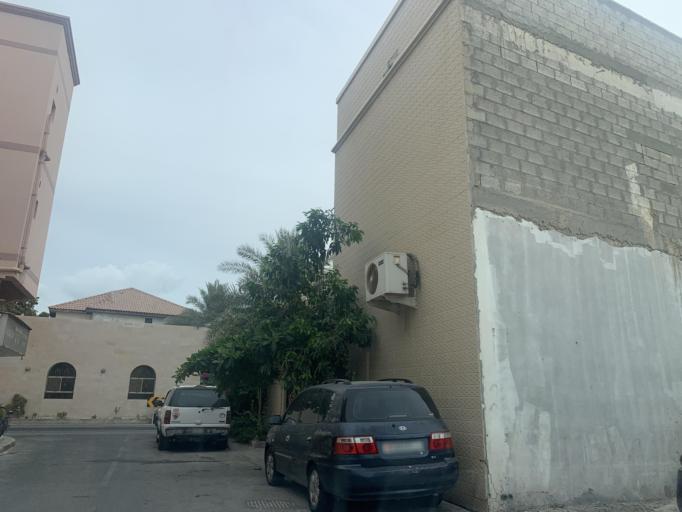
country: BH
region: Muharraq
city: Al Hadd
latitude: 26.2748
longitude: 50.6498
